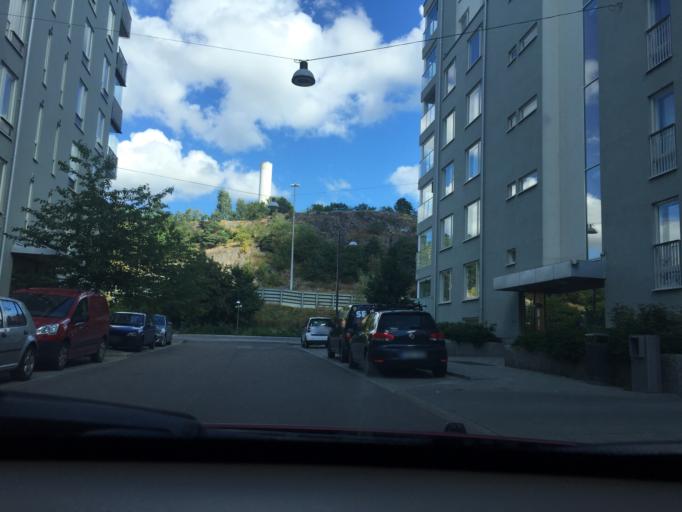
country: SE
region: Stockholm
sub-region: Stockholms Kommun
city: OEstermalm
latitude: 59.3071
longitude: 18.1096
